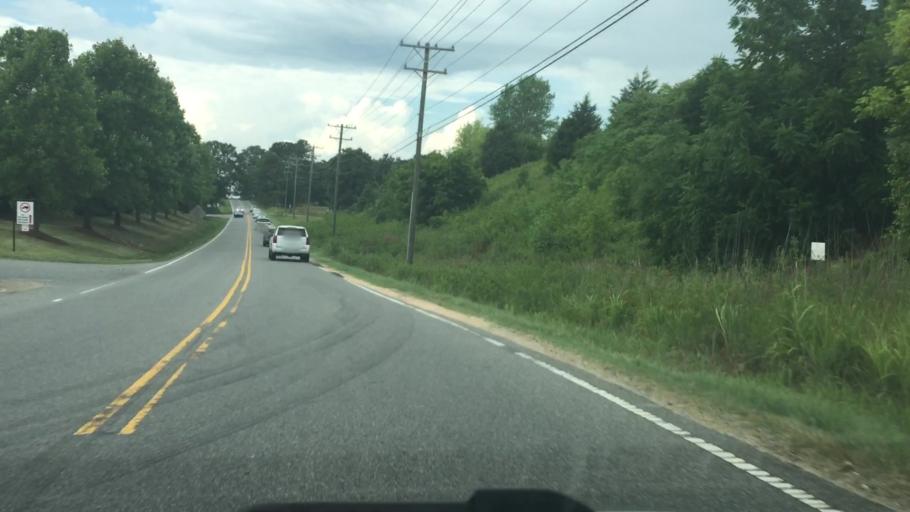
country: US
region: North Carolina
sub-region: Cabarrus County
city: Harrisburg
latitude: 35.4124
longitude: -80.7098
